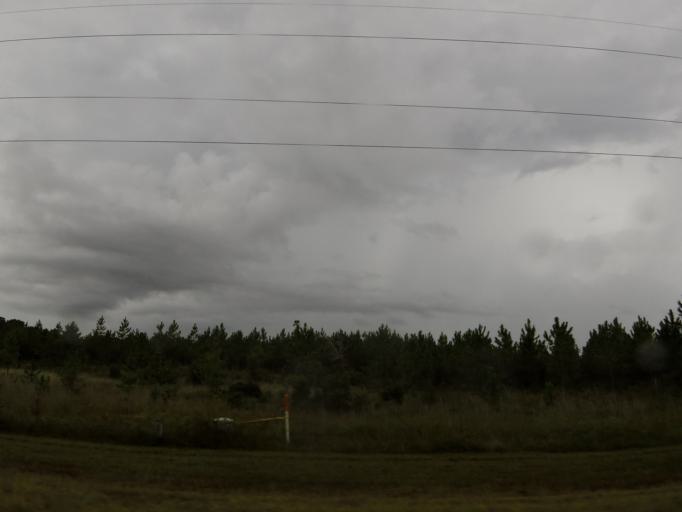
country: US
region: Florida
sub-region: Baker County
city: Macclenny
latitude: 30.4492
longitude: -82.0739
